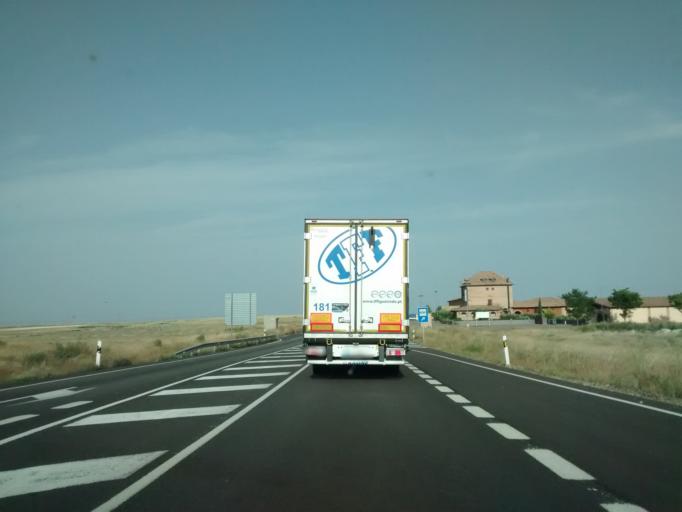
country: ES
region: Aragon
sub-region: Provincia de Zaragoza
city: Albeta
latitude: 41.8309
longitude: -1.5021
